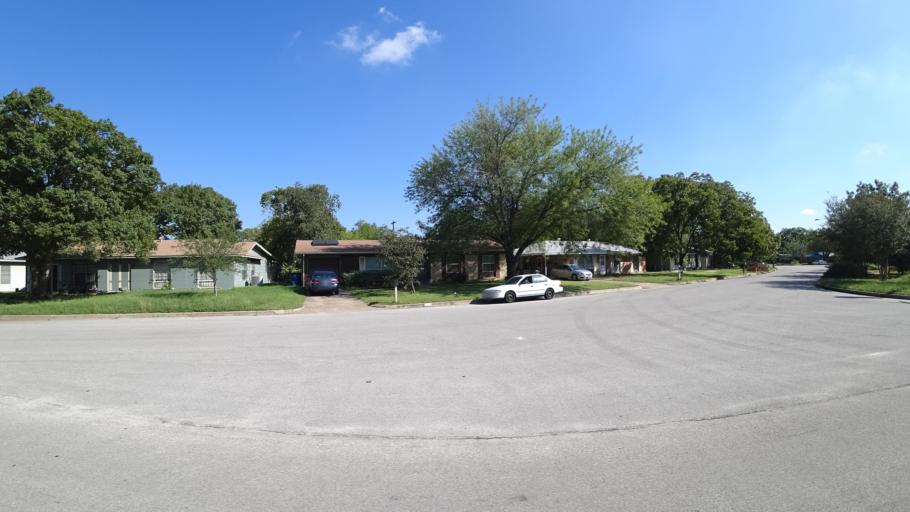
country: US
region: Texas
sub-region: Travis County
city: Austin
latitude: 30.3397
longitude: -97.7121
